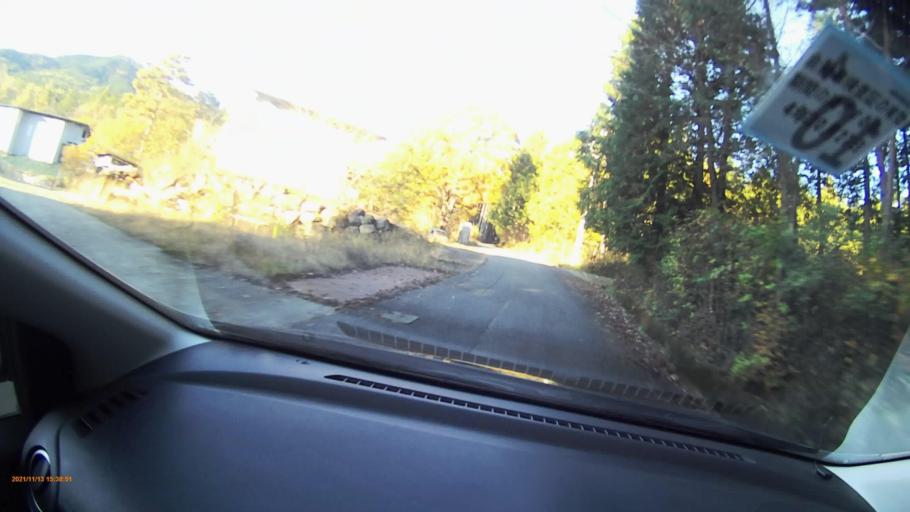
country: JP
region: Gifu
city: Nakatsugawa
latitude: 35.5846
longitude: 137.3818
